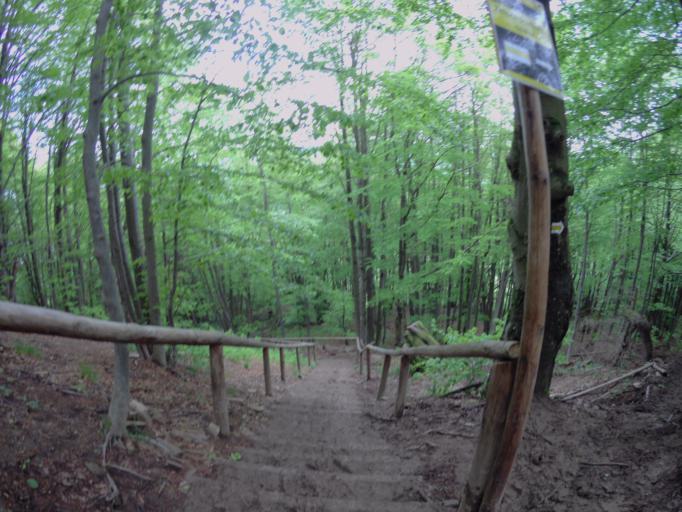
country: PL
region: Subcarpathian Voivodeship
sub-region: Powiat bieszczadzki
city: Lutowiska
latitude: 49.1509
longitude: 22.5560
